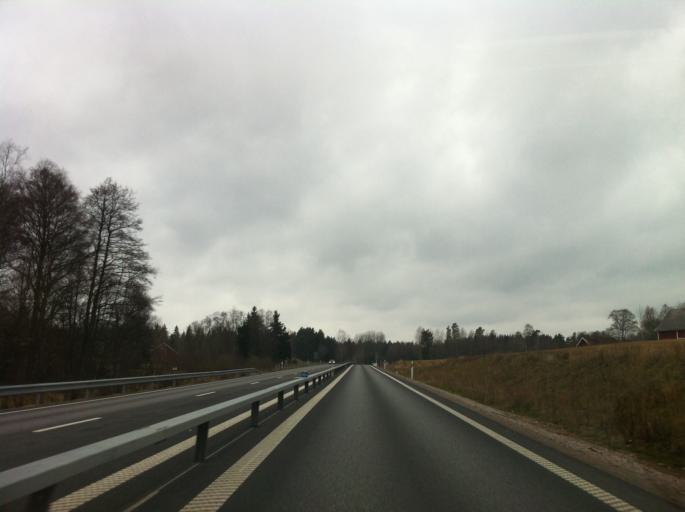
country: SE
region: Joenkoeping
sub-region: Vetlanda Kommun
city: Vetlanda
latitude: 57.4250
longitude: 15.1375
